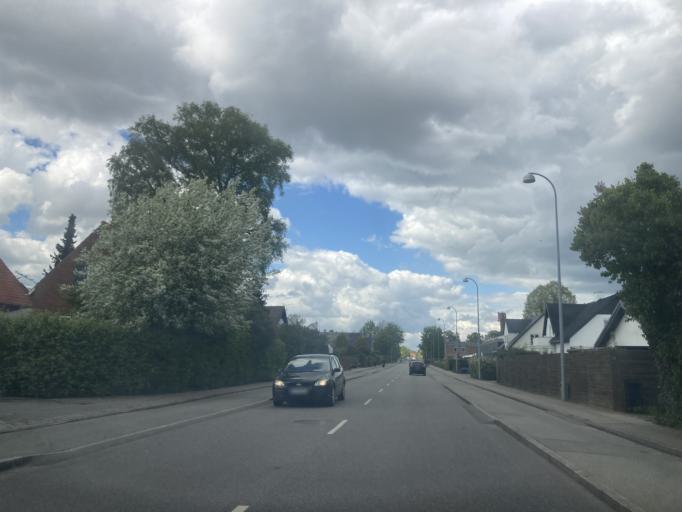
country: DK
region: Capital Region
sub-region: Gladsaxe Municipality
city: Buddinge
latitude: 55.7575
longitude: 12.4840
